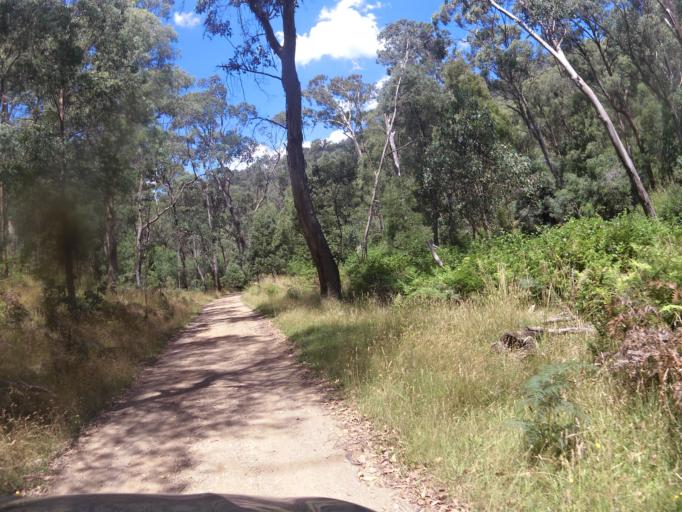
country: AU
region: Victoria
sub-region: Alpine
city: Mount Beauty
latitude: -36.7800
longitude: 147.0672
